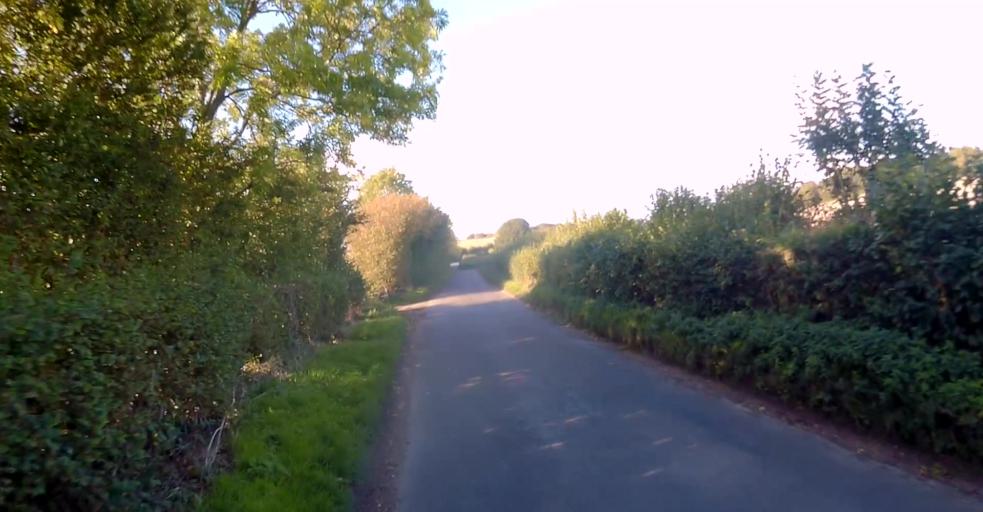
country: GB
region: England
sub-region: Hampshire
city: Long Sutton
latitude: 51.2296
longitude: -0.9254
